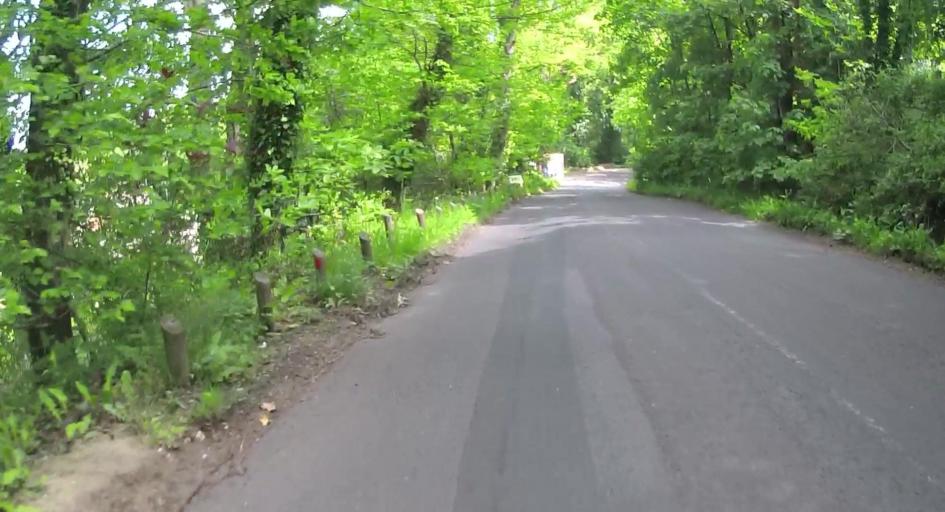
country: GB
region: England
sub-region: Surrey
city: Farnham
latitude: 51.1879
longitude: -0.8030
